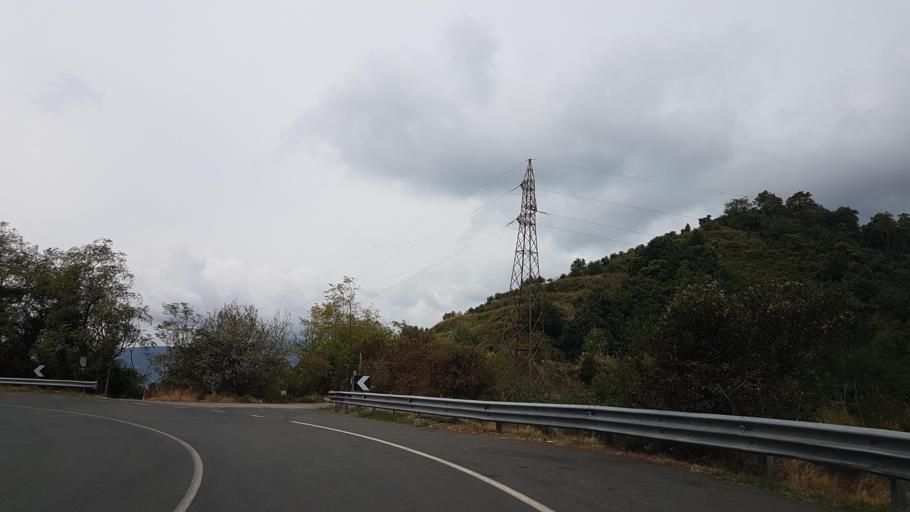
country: IT
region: Liguria
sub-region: Provincia di Genova
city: Moneglia
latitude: 44.2583
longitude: 9.4726
